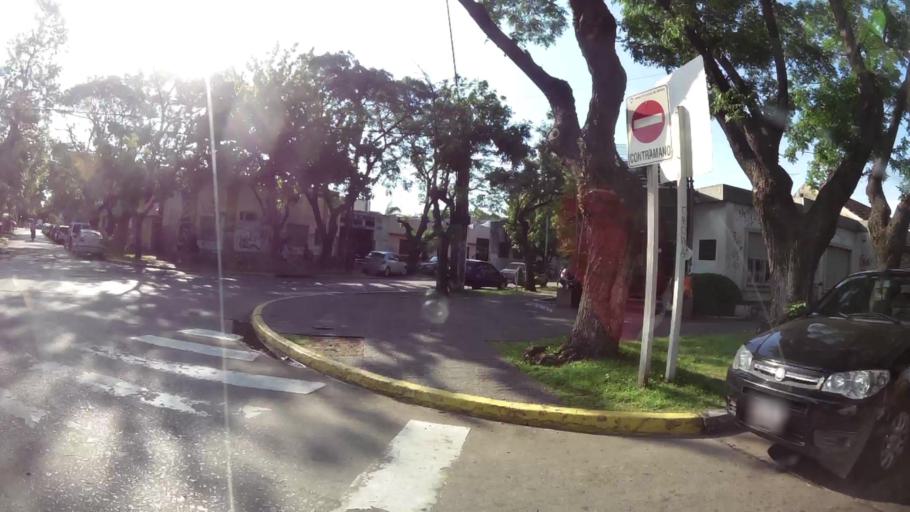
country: AR
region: Buenos Aires
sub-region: Partido de Merlo
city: Merlo
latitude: -34.6720
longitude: -58.7231
